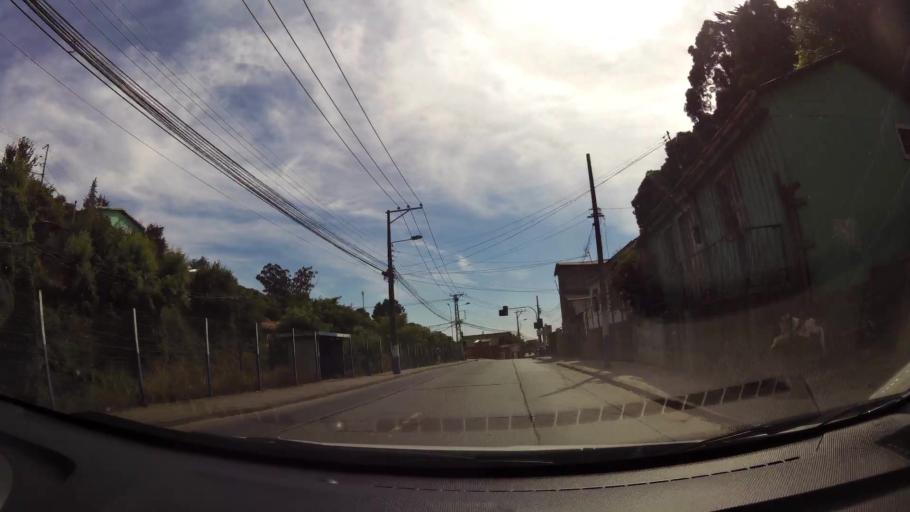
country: CL
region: Biobio
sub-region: Provincia de Concepcion
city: Talcahuano
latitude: -36.7157
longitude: -73.1181
